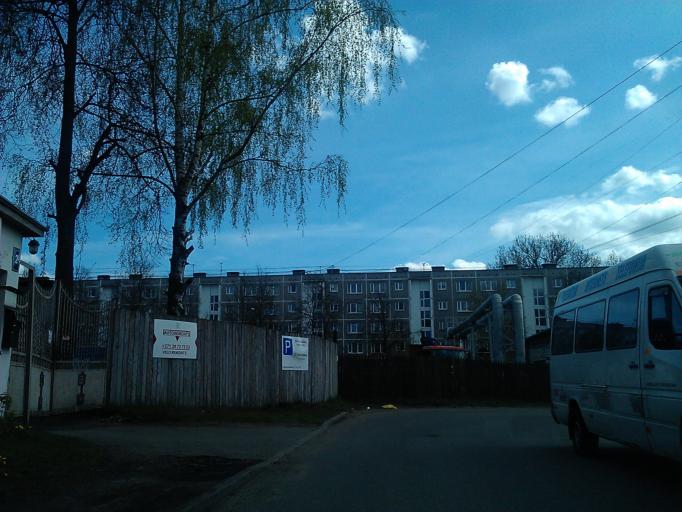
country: LV
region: Kekava
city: Balozi
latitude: 56.9086
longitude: 24.1918
